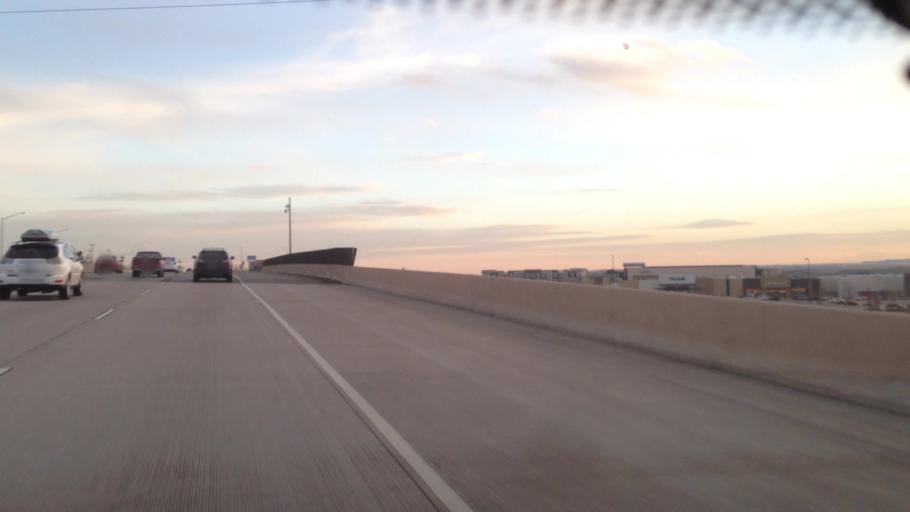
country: US
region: Colorado
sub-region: Arapahoe County
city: Dove Valley
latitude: 39.5957
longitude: -104.8028
